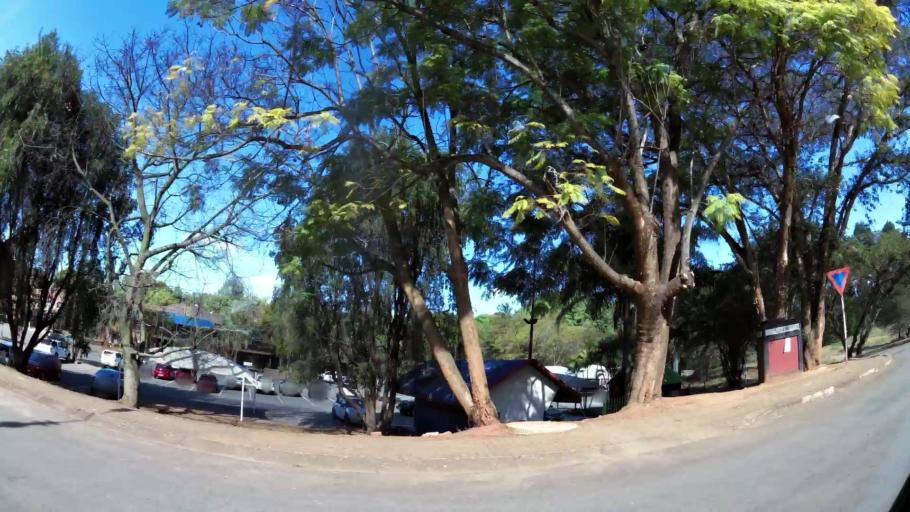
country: ZA
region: Limpopo
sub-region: Mopani District Municipality
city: Tzaneen
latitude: -23.8166
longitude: 30.1575
